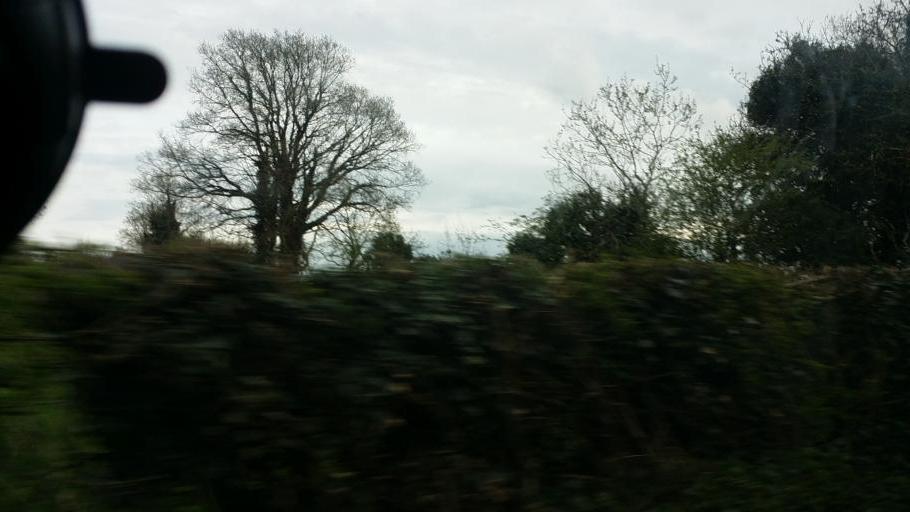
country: IE
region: Ulster
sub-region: An Cabhan
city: Ballyconnell
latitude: 54.0893
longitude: -7.5368
